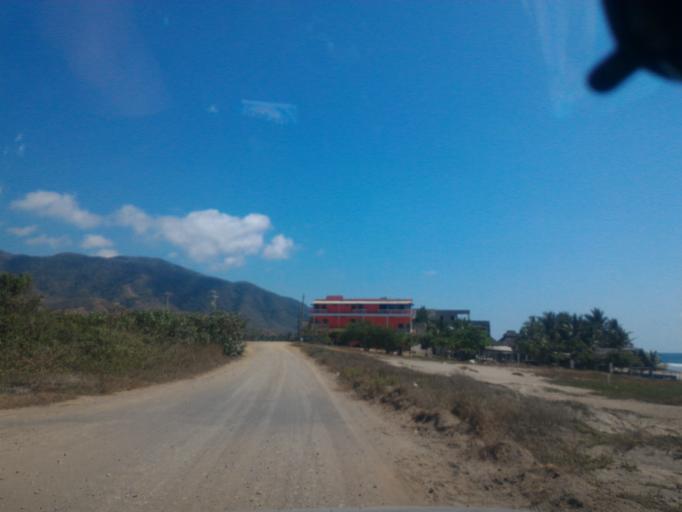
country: MX
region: Michoacan
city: Coahuayana Viejo
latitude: 18.5890
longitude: -103.6837
